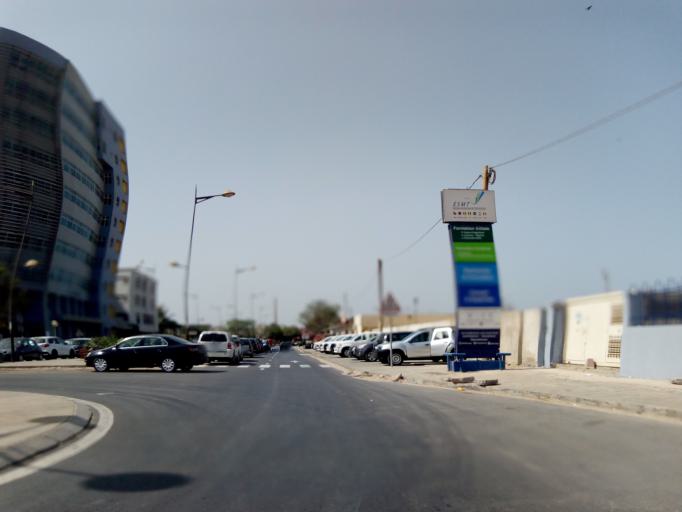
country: SN
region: Dakar
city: Dakar
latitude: 14.6997
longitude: -17.4502
